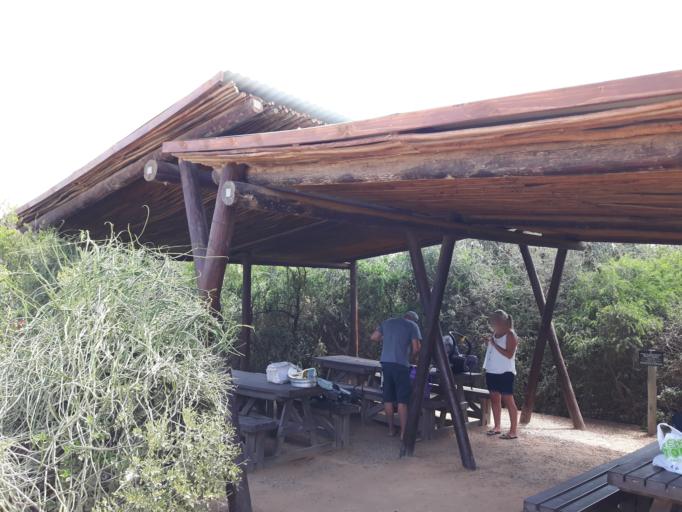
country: ZA
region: Eastern Cape
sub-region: Cacadu District Municipality
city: Kirkwood
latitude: -33.5166
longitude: 25.7612
